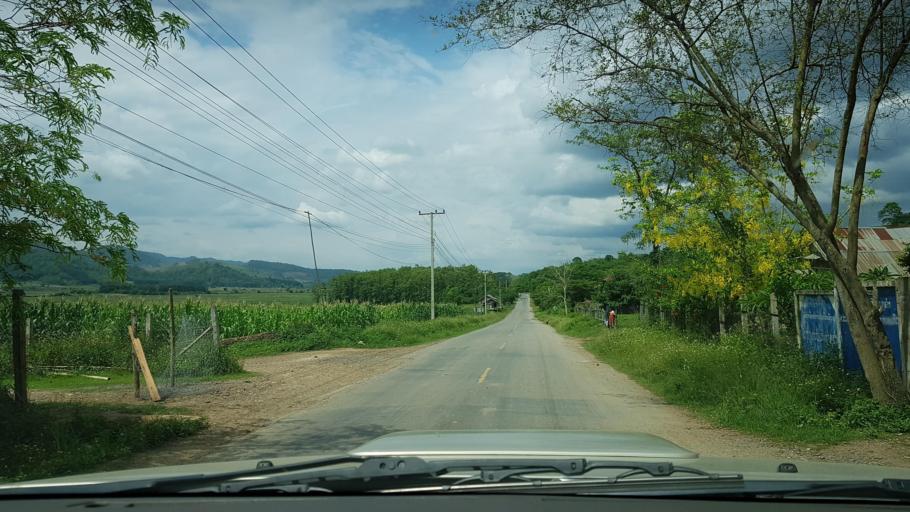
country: LA
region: Loungnamtha
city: Muang Nale
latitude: 20.2663
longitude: 101.5967
